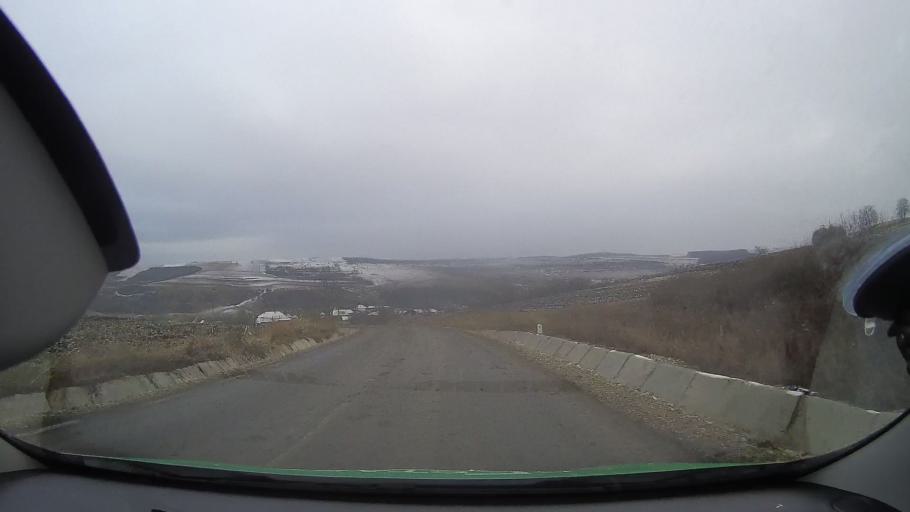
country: RO
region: Alba
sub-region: Comuna Farau
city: Farau
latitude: 46.3905
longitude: 24.0205
